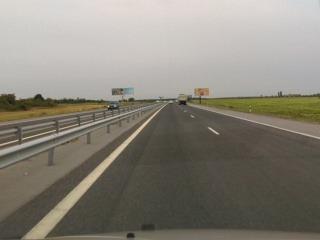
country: BG
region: Stara Zagora
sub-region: Obshtina Stara Zagora
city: Stara Zagora
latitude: 42.3197
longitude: 25.5605
